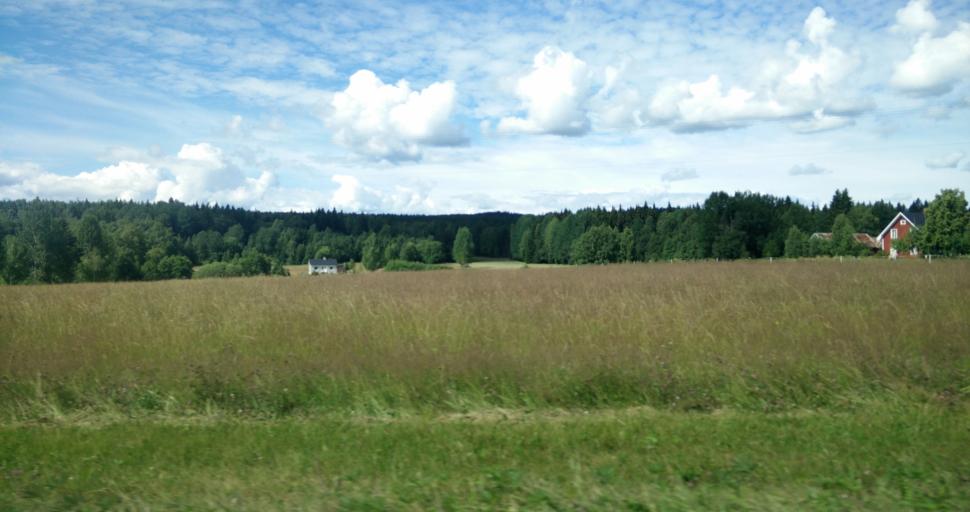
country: SE
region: Vaermland
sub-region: Hagfors Kommun
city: Ekshaerad
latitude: 60.1031
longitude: 13.4510
